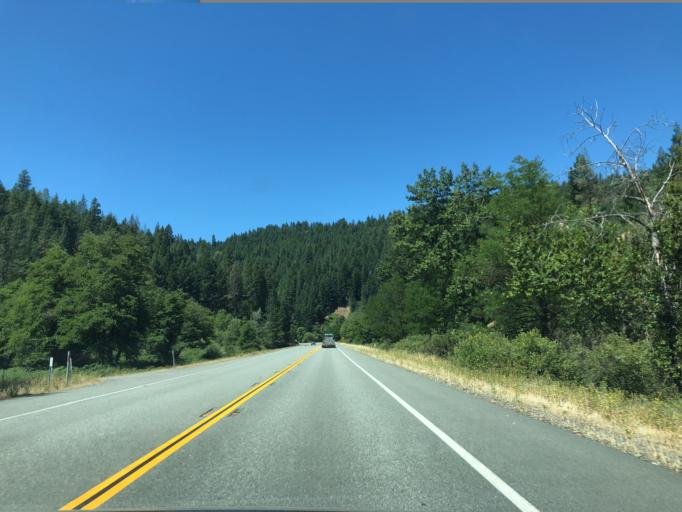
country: US
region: California
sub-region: Trinity County
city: Weaverville
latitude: 40.6819
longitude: -122.9379
